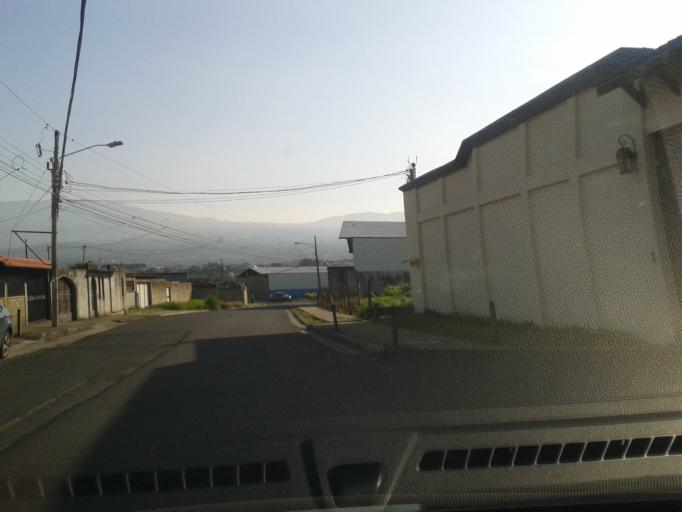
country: CR
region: Heredia
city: San Francisco
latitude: 9.9941
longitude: -84.1342
